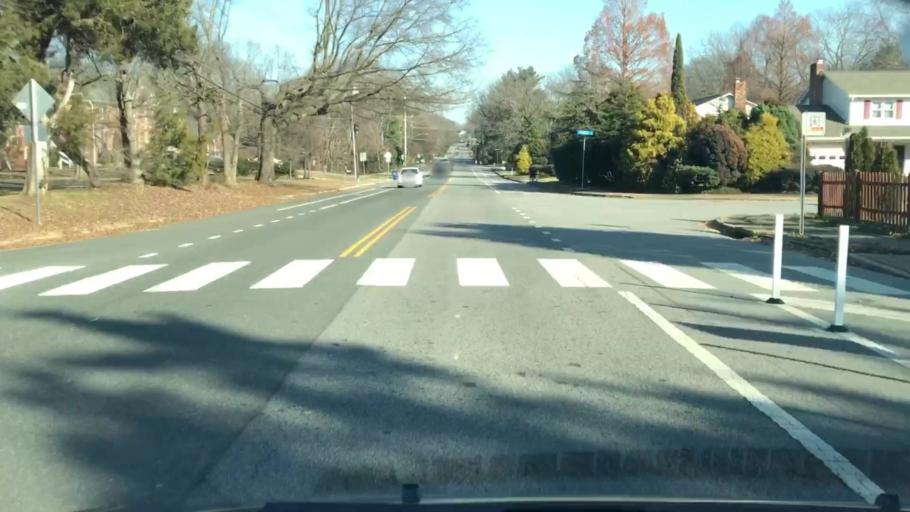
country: US
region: Virginia
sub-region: Fairfax County
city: Hybla Valley
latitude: 38.7442
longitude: -77.0744
